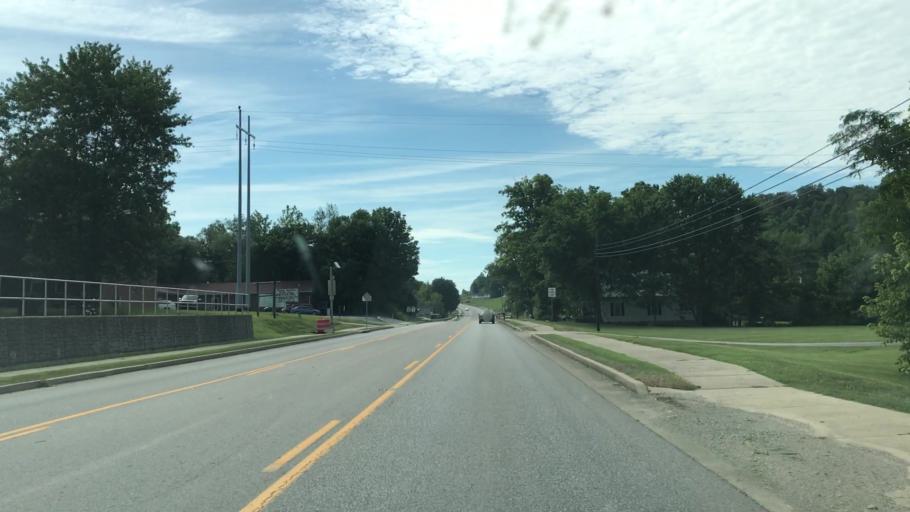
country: US
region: Kentucky
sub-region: Edmonson County
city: Brownsville
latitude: 37.1891
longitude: -86.2540
